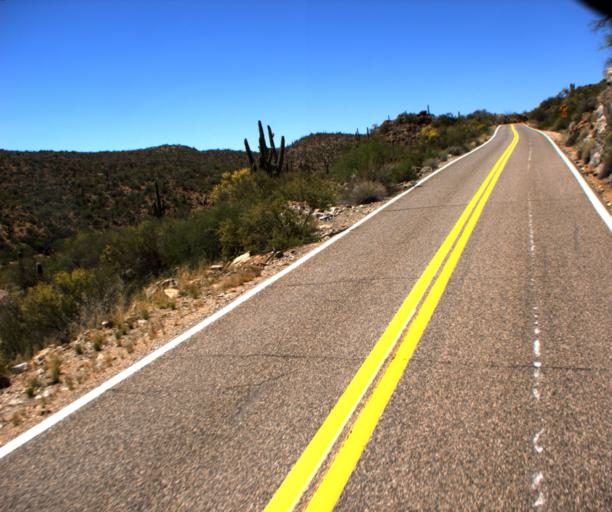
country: US
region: Arizona
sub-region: Yavapai County
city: Bagdad
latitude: 34.5087
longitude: -113.0757
